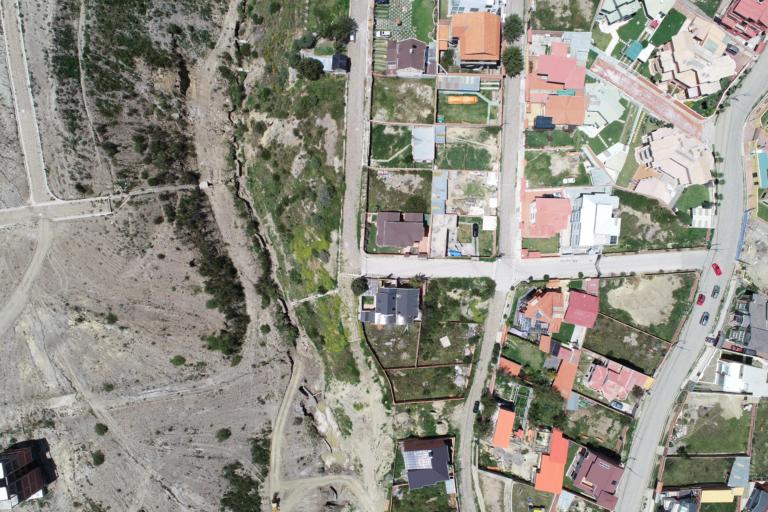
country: BO
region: La Paz
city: La Paz
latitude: -16.5220
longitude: -68.0539
